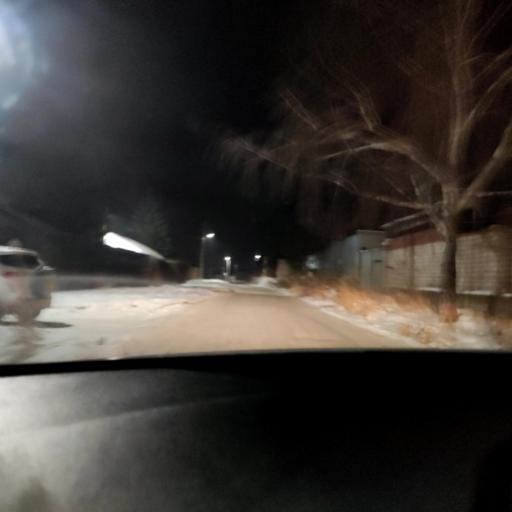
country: RU
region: Tatarstan
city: Stolbishchi
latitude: 55.7562
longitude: 49.2537
